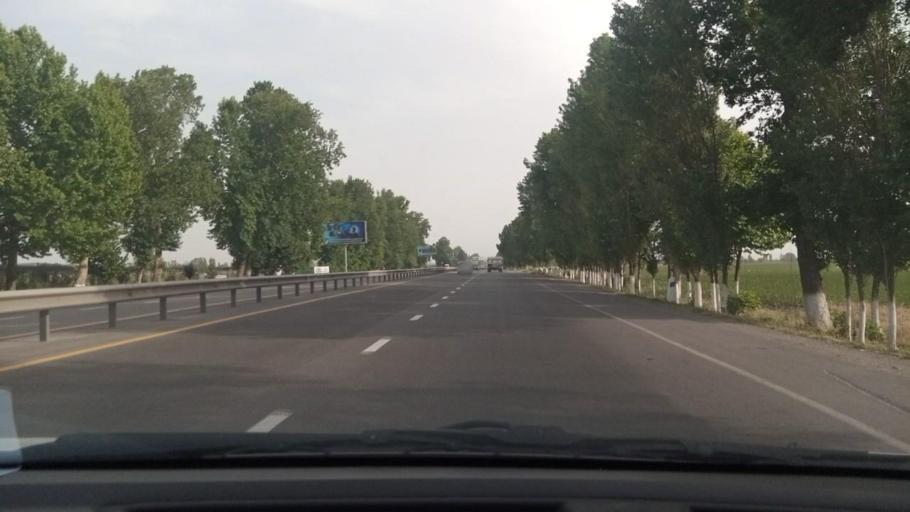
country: UZ
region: Toshkent Shahri
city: Bektemir
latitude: 41.2355
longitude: 69.4021
